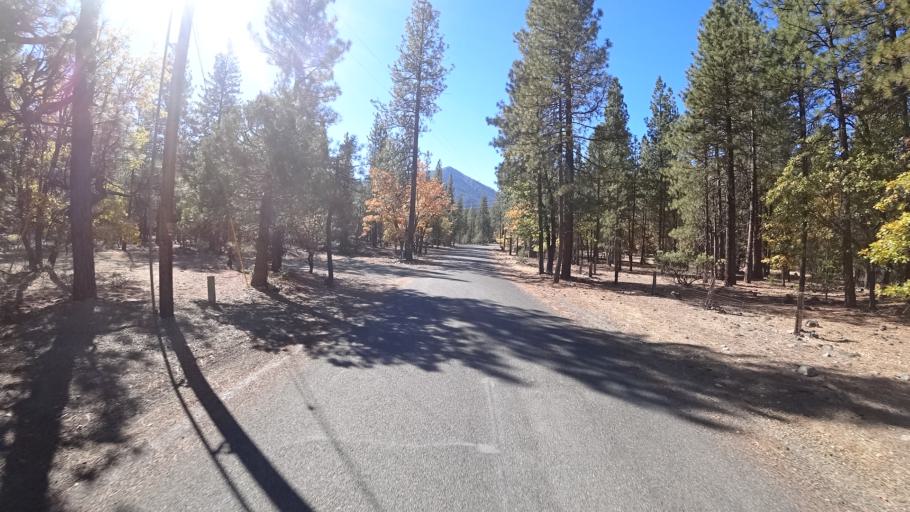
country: US
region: California
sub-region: Siskiyou County
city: Yreka
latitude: 41.5339
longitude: -122.9590
